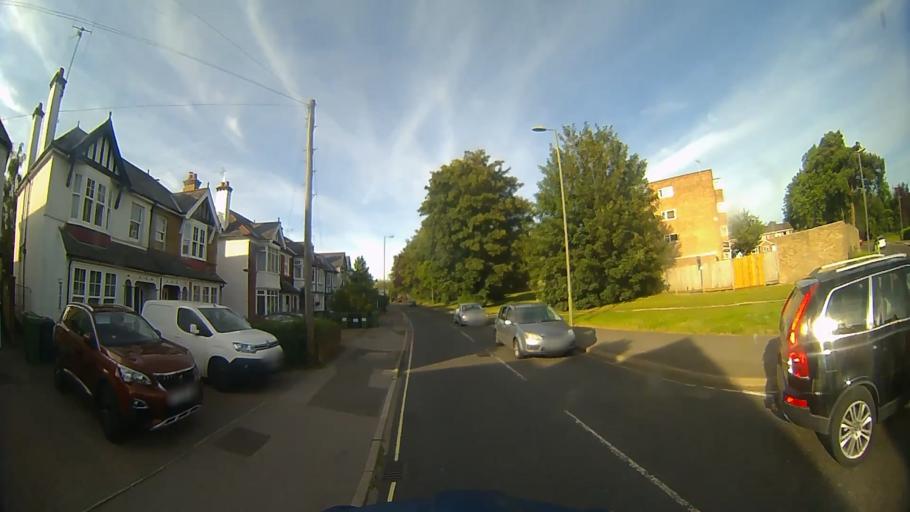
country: GB
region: England
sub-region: Hampshire
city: Basingstoke
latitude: 51.2589
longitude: -1.0964
